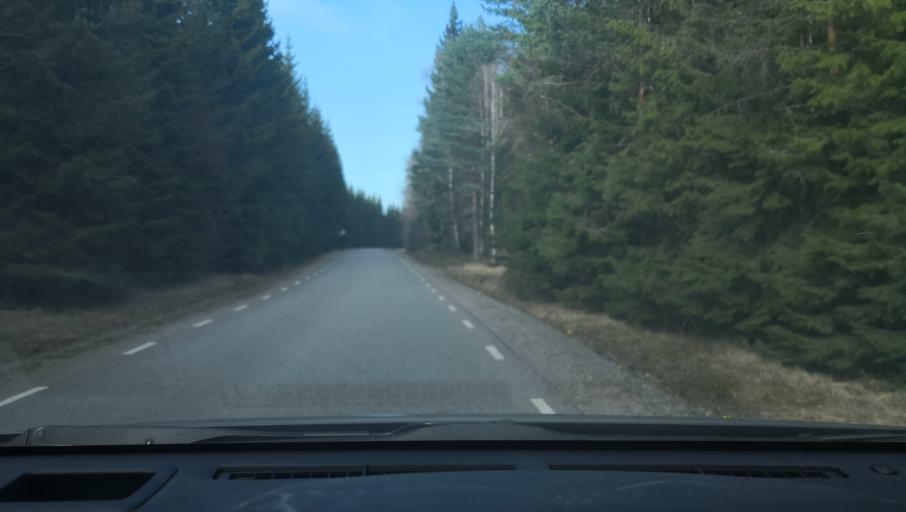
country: SE
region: Uppsala
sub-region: Heby Kommun
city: Heby
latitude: 59.9081
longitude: 16.8224
